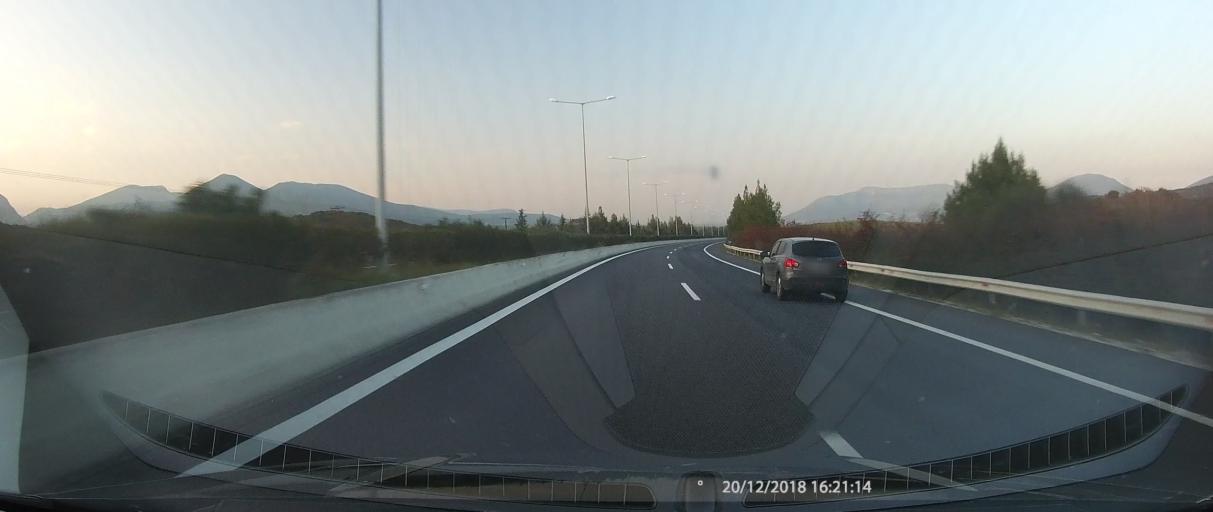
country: GR
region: Thessaly
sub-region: Nomos Magnisias
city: Pteleos
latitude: 39.0432
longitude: 22.8945
